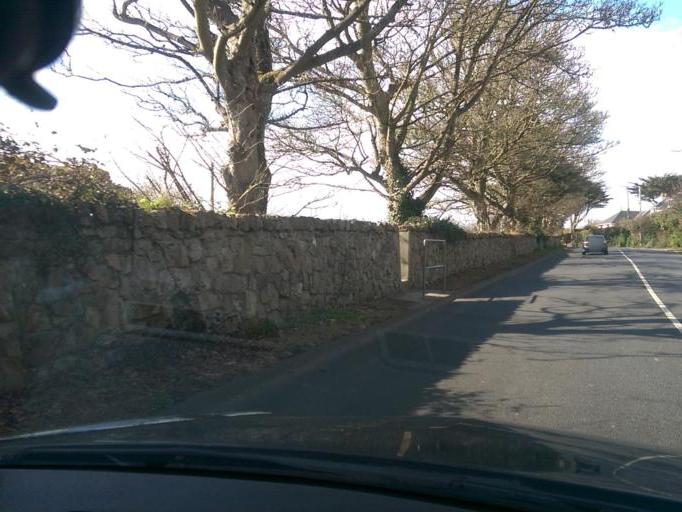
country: IE
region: Leinster
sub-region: Fingal County
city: Howth
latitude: 53.3708
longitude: -6.0867
